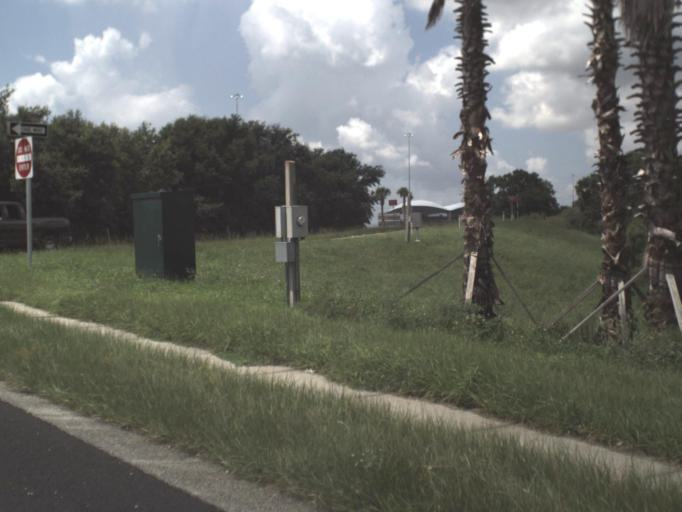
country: US
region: Florida
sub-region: Hillsborough County
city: East Lake-Orient Park
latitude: 27.9986
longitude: -82.3573
